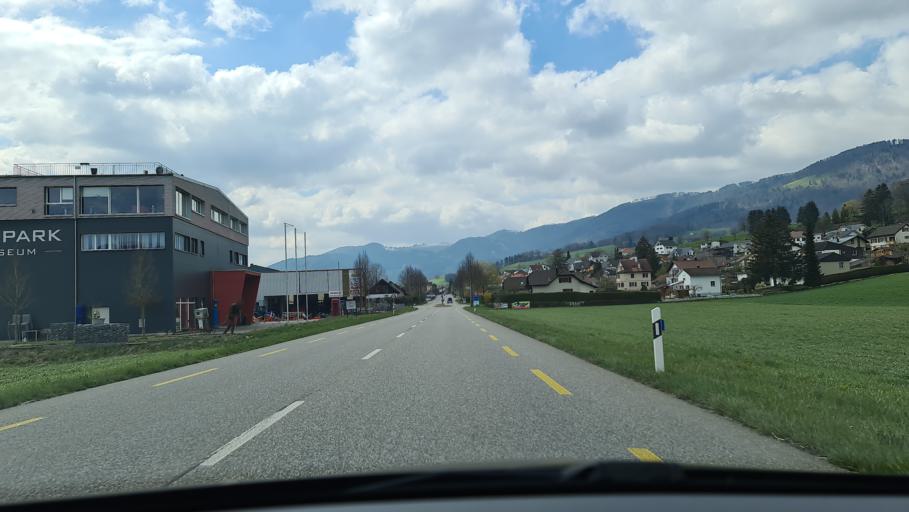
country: CH
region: Solothurn
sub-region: Bezirk Thal
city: Laupersdorf
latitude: 47.3122
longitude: 7.6654
